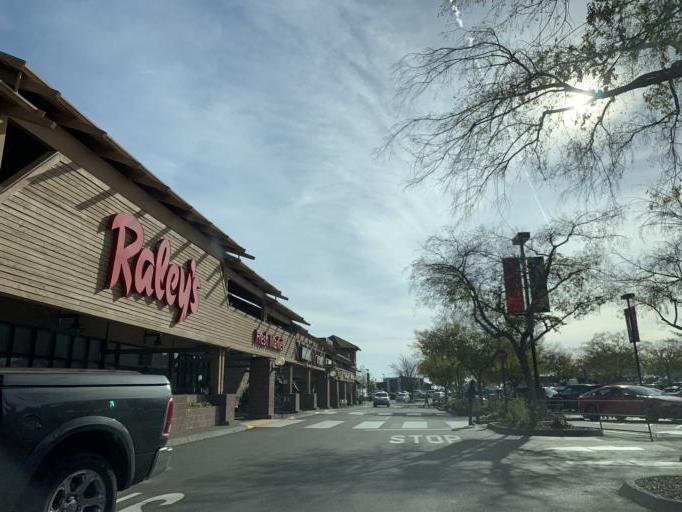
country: US
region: California
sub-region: El Dorado County
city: El Dorado Hills
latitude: 38.6558
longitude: -121.0701
